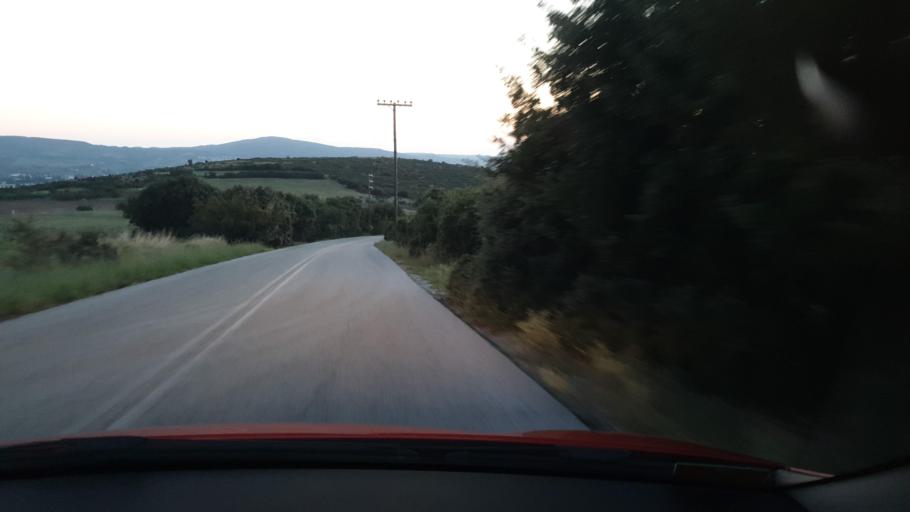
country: GR
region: Central Macedonia
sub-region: Nomos Thessalonikis
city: Vasilika
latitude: 40.5084
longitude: 23.1502
